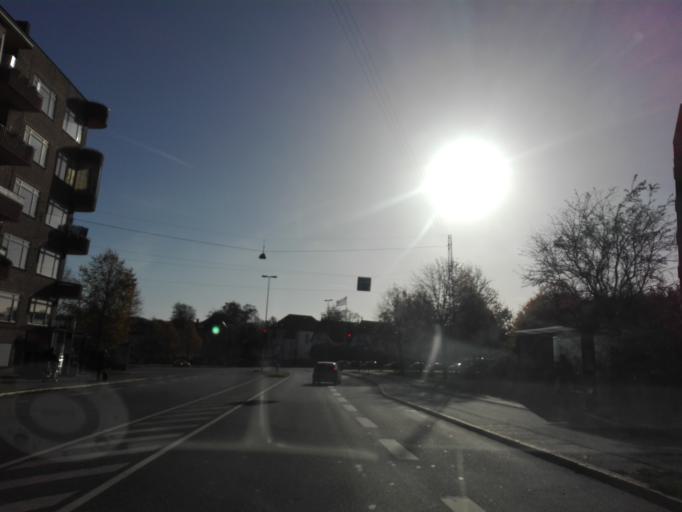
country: DK
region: Central Jutland
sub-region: Arhus Kommune
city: Arhus
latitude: 56.1426
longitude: 10.2040
